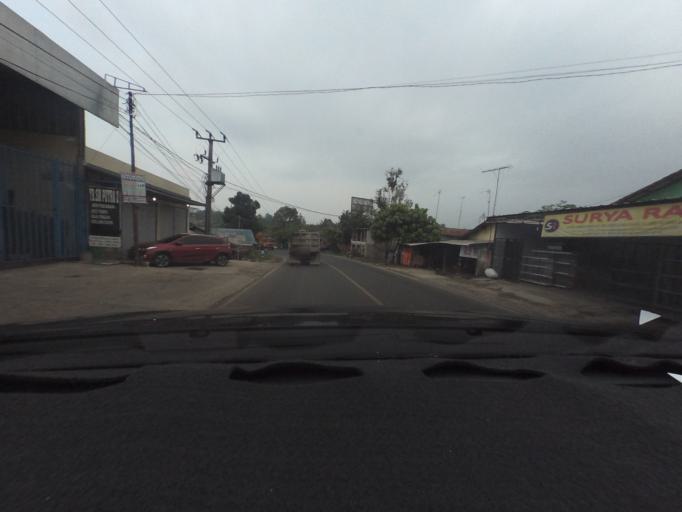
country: ID
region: West Java
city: Cicurug
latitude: -6.8133
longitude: 106.7692
